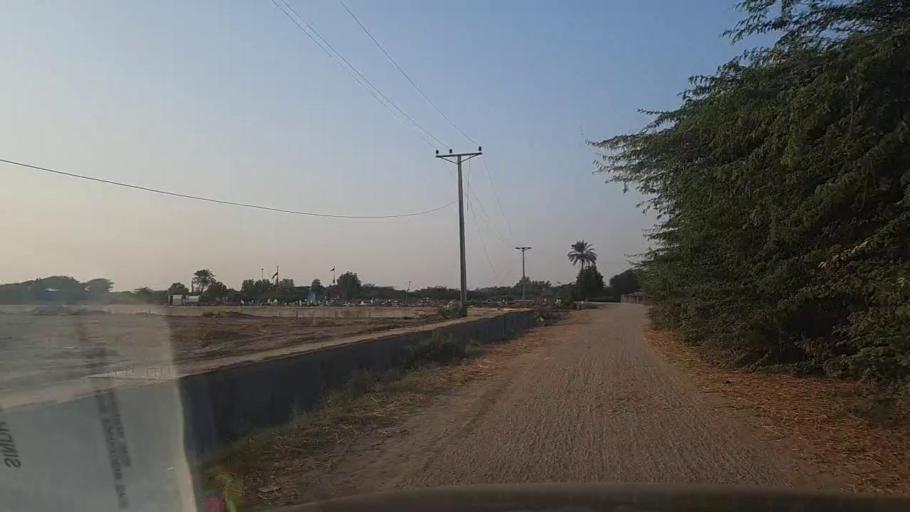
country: PK
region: Sindh
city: Keti Bandar
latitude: 24.3072
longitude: 67.6031
